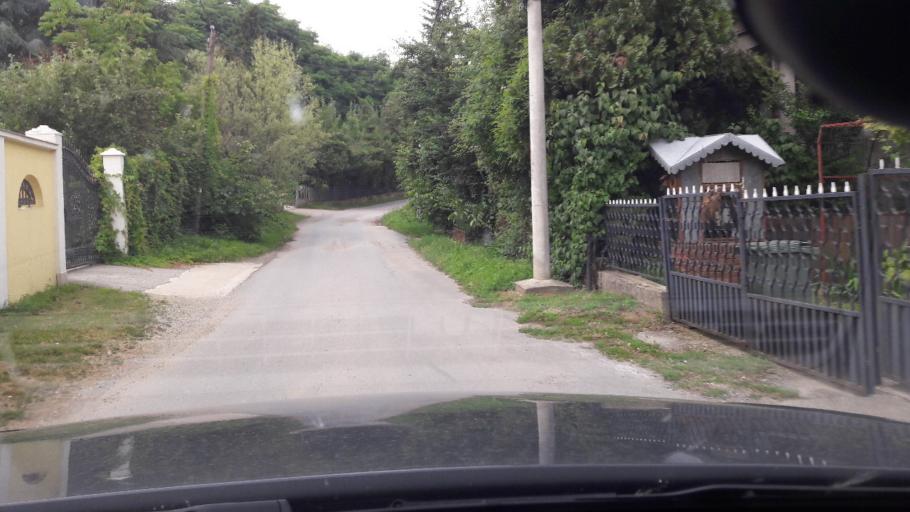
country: RS
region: Central Serbia
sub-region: Belgrade
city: Grocka
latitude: 44.6521
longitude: 20.5977
